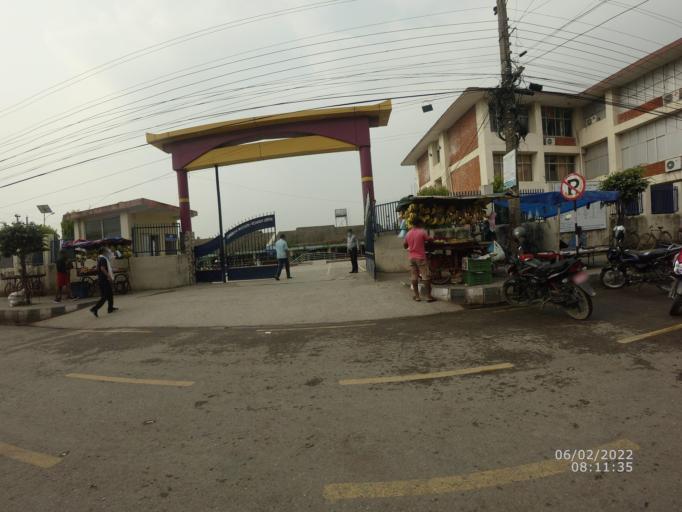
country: NP
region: Western Region
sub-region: Lumbini Zone
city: Bhairahawa
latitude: 27.4972
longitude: 83.4584
